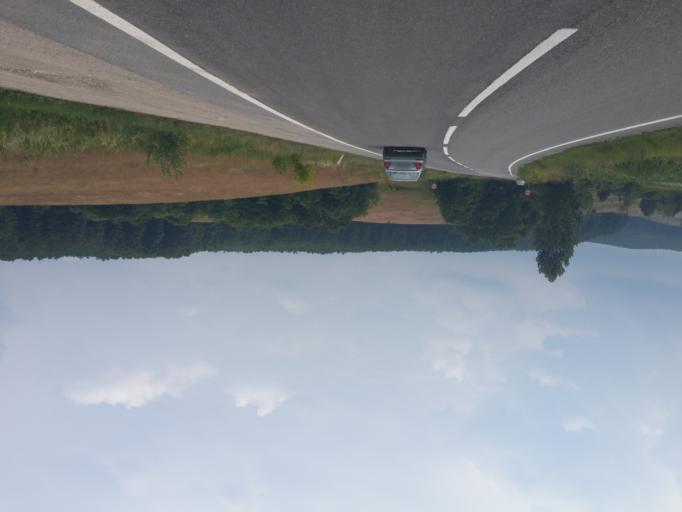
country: RO
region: Salaj
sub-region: Comuna Romanasi
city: Romanasi
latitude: 47.1196
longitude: 23.1646
